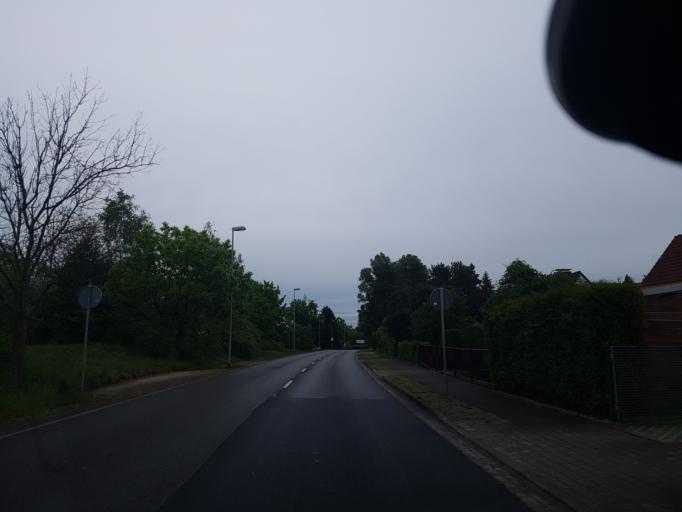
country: DE
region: Brandenburg
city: Neupetershain
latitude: 51.6233
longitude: 14.1586
